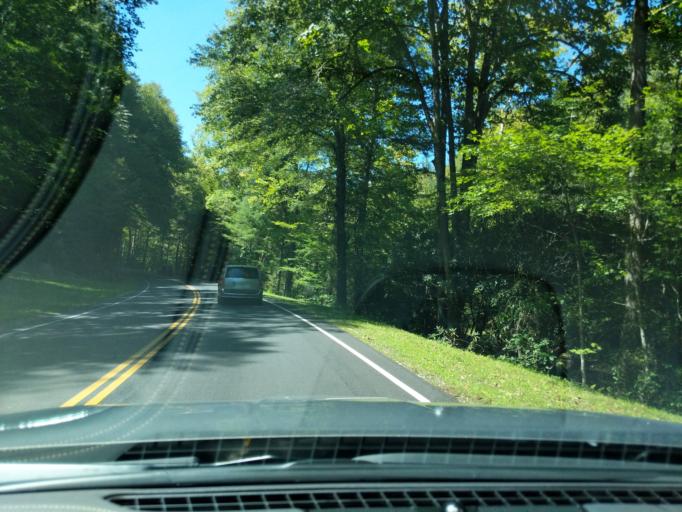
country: US
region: North Carolina
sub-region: Swain County
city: Cherokee
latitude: 35.5544
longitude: -83.3106
